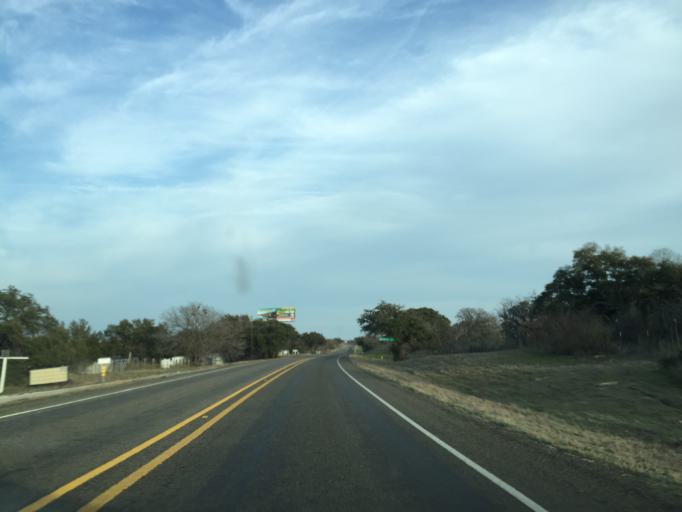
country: US
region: Texas
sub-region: Llano County
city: Llano
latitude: 30.7616
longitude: -98.6307
